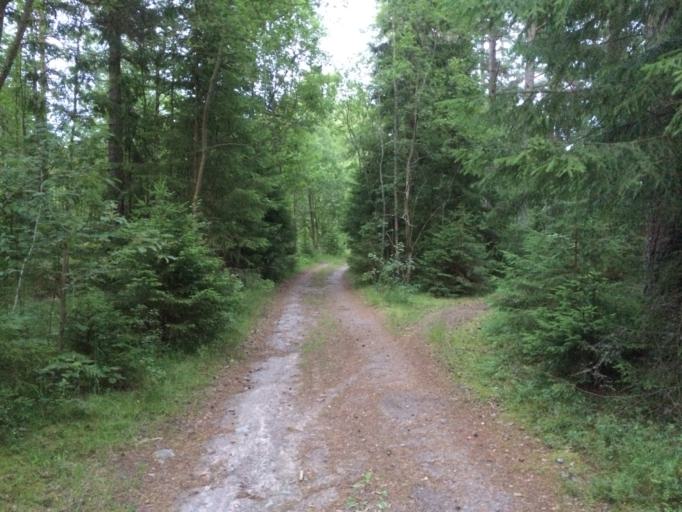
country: SE
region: Vaestra Goetaland
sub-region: Karlsborgs Kommun
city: Karlsborg
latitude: 58.5602
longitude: 14.5075
